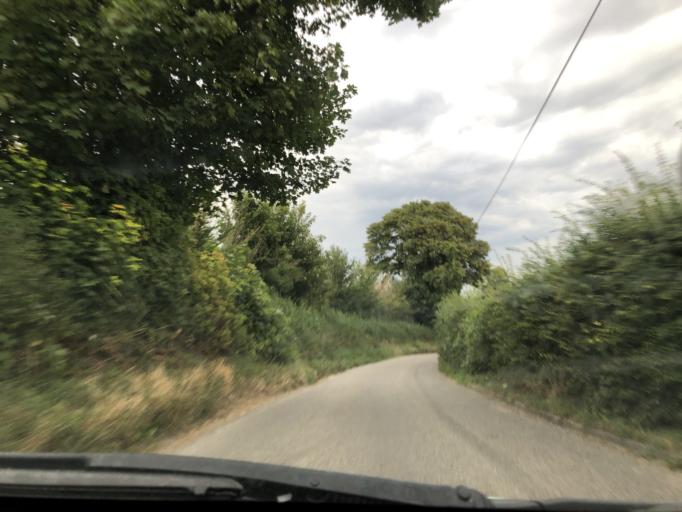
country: GB
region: England
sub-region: Kent
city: Shoreham
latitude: 51.3226
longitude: 0.1663
